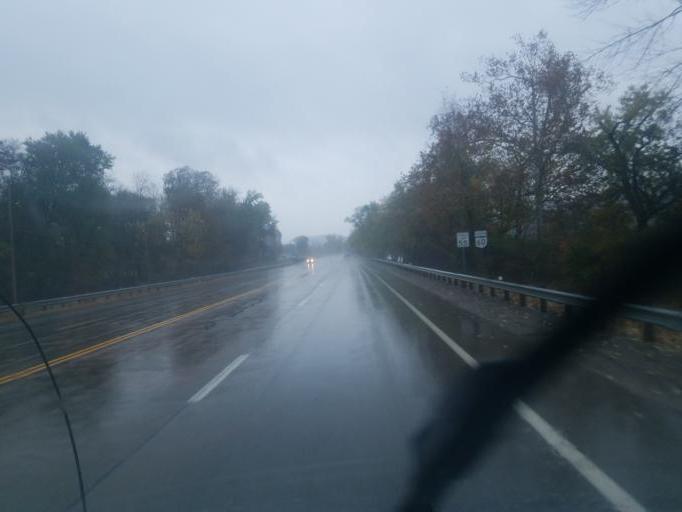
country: US
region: Ohio
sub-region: Muskingum County
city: South Zanesville
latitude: 39.8892
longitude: -81.9919
